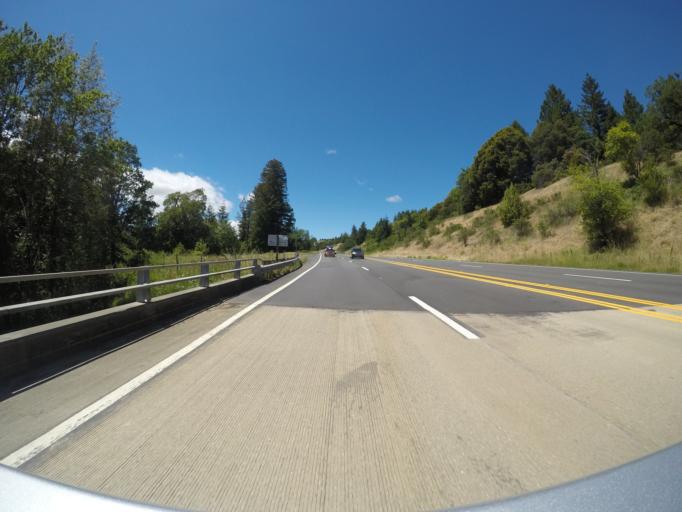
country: US
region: California
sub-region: Humboldt County
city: Redway
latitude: 39.9590
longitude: -123.7824
